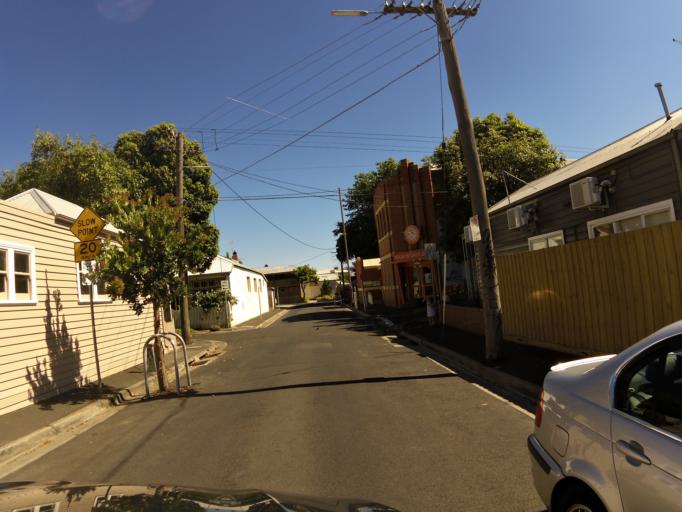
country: AU
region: Victoria
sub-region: Yarra
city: Richmond
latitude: -37.8222
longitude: 145.0059
